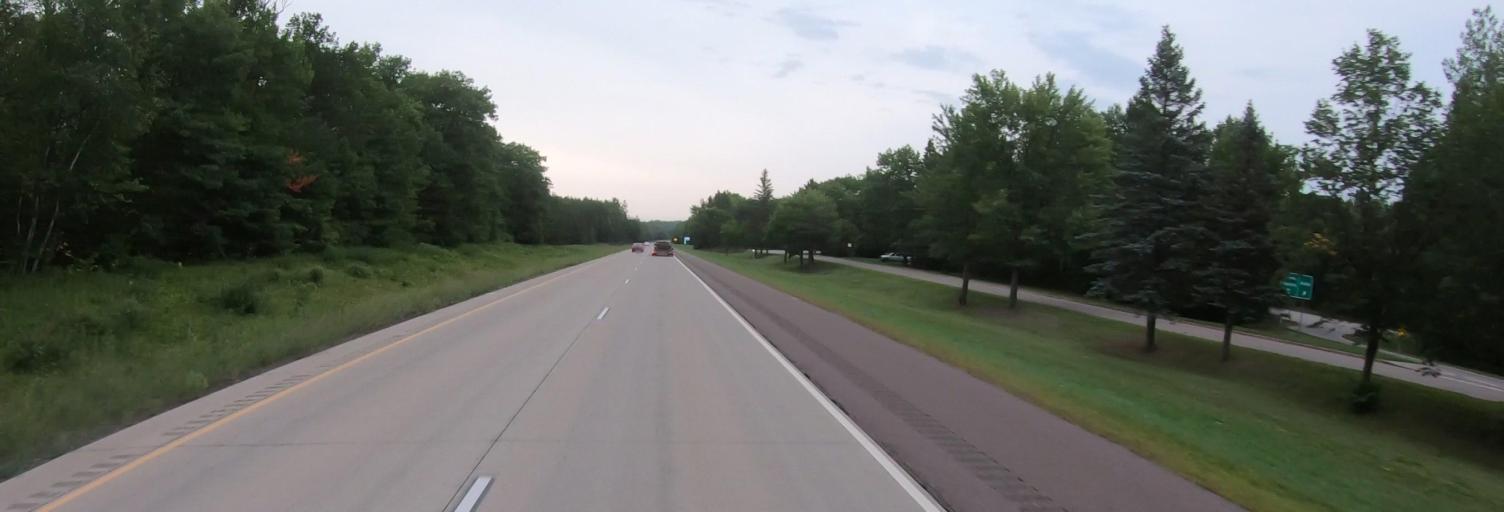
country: US
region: Minnesota
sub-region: Pine County
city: Sandstone
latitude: 46.2103
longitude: -92.8379
